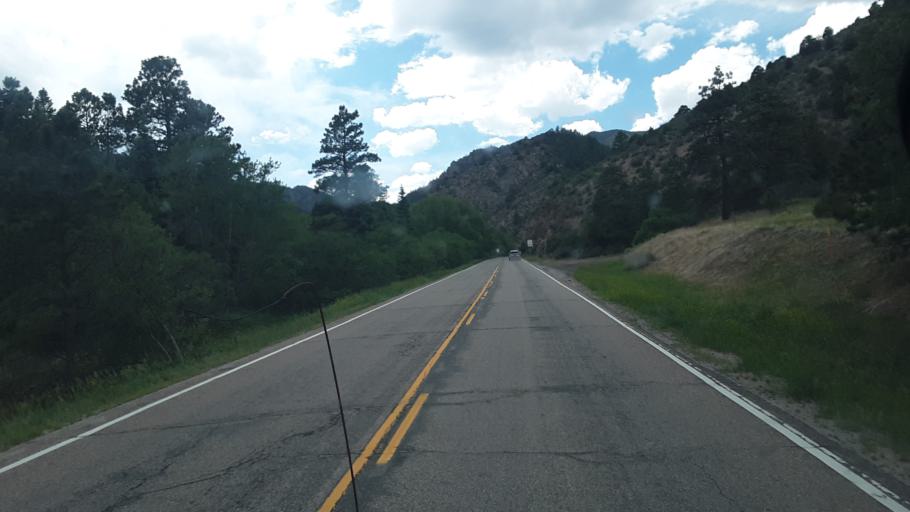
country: US
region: Colorado
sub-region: Fremont County
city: Florence
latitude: 38.1763
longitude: -105.1346
